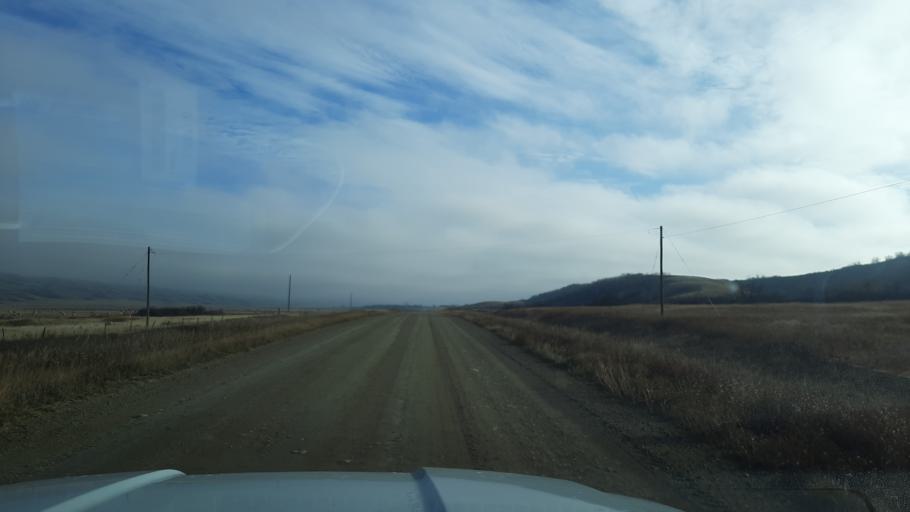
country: CA
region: Saskatchewan
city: Pilot Butte
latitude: 50.7844
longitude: -104.2107
